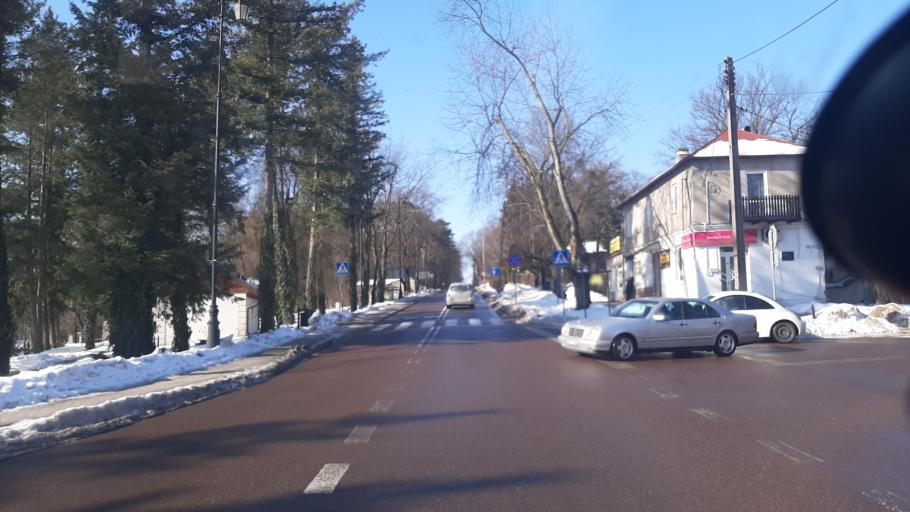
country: PL
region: Lublin Voivodeship
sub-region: Powiat pulawski
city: Naleczow
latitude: 51.2879
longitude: 22.2147
